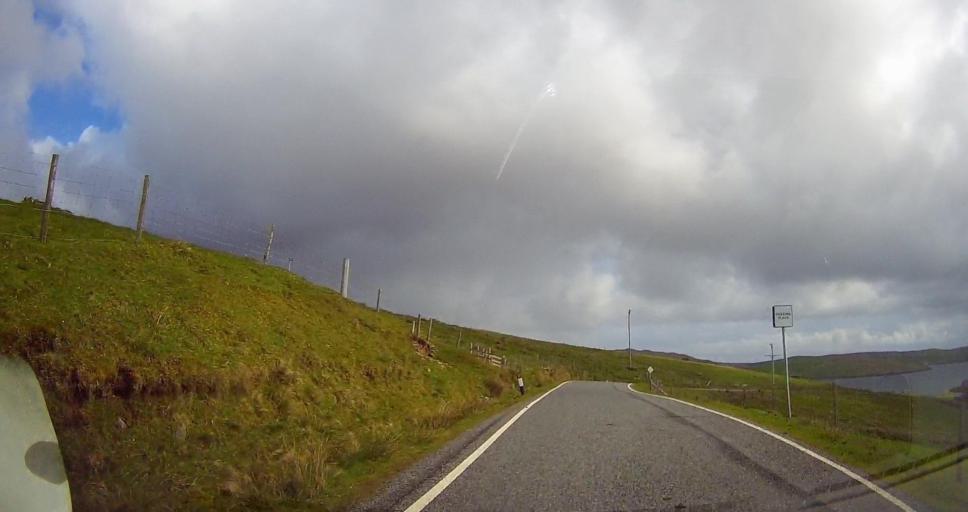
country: GB
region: Scotland
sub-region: Shetland Islands
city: Lerwick
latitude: 60.5287
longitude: -1.3671
